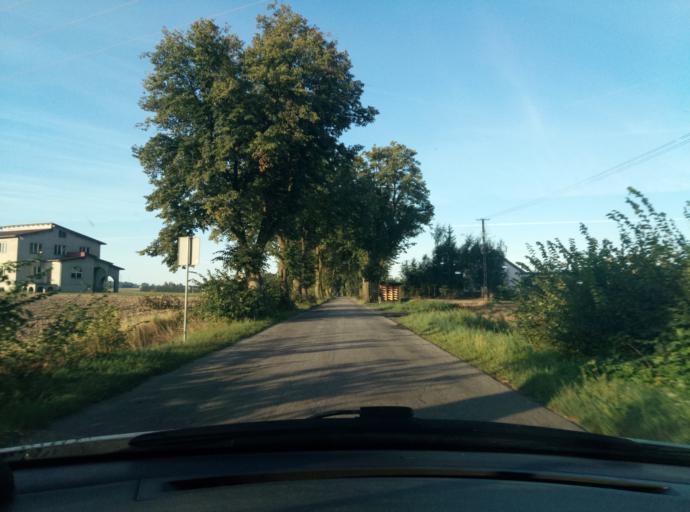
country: PL
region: Kujawsko-Pomorskie
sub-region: Powiat brodnicki
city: Jablonowo Pomorskie
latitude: 53.4050
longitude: 19.1708
